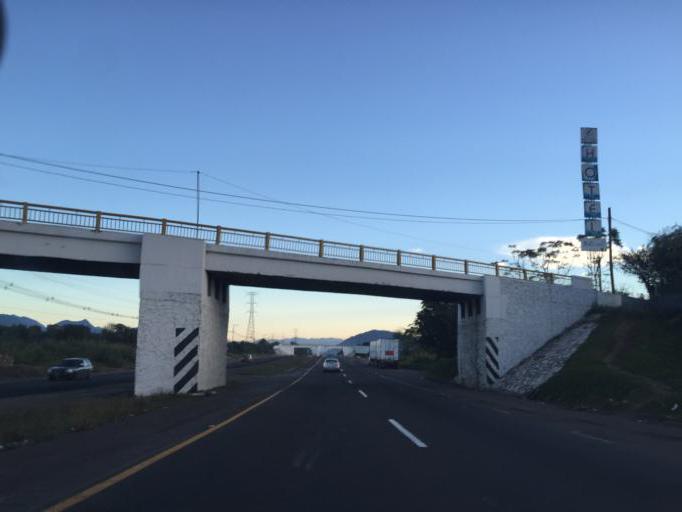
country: MX
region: Veracruz
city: Jalapilla
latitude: 18.8397
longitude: -97.0793
